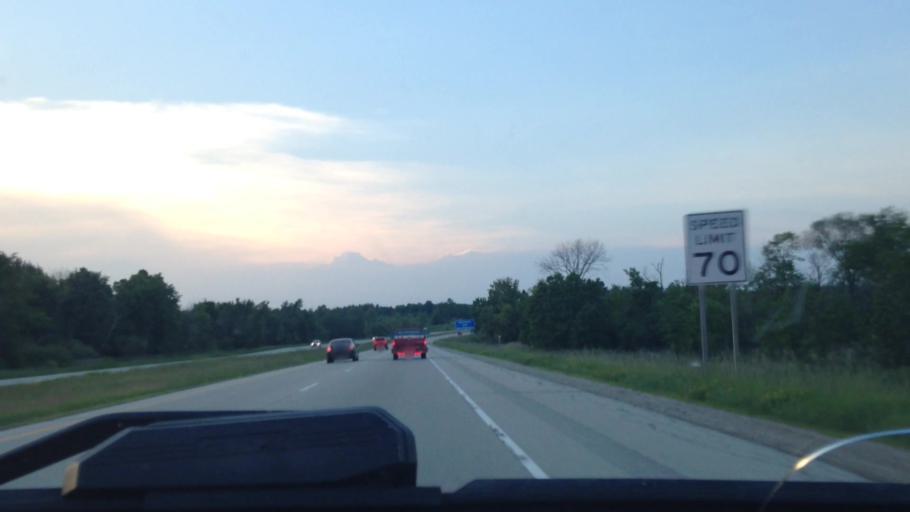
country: US
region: Wisconsin
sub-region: Washington County
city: Jackson
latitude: 43.3655
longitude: -88.1927
